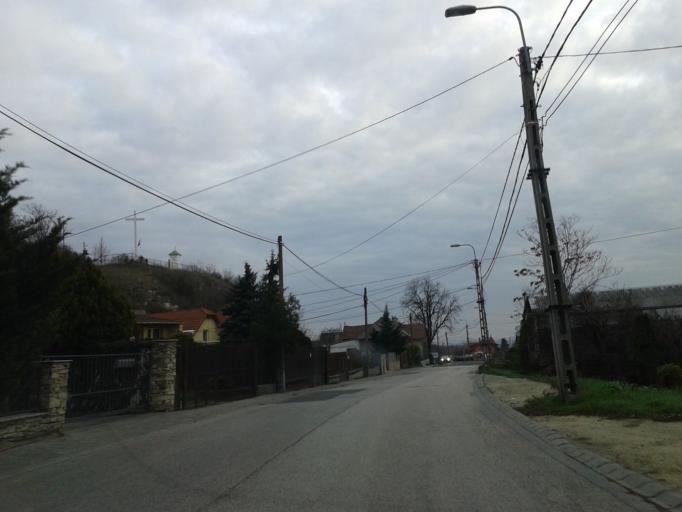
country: HU
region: Pest
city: Diosd
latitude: 47.4114
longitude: 18.9899
